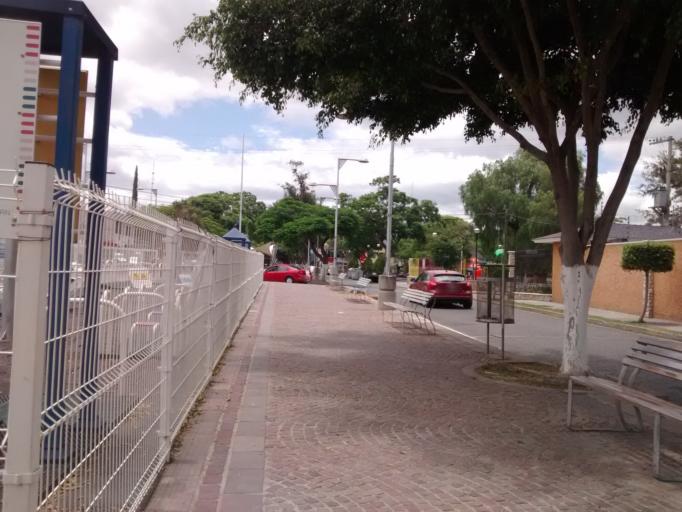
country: MX
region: Puebla
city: Tehuacan
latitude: 18.4521
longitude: -97.3927
